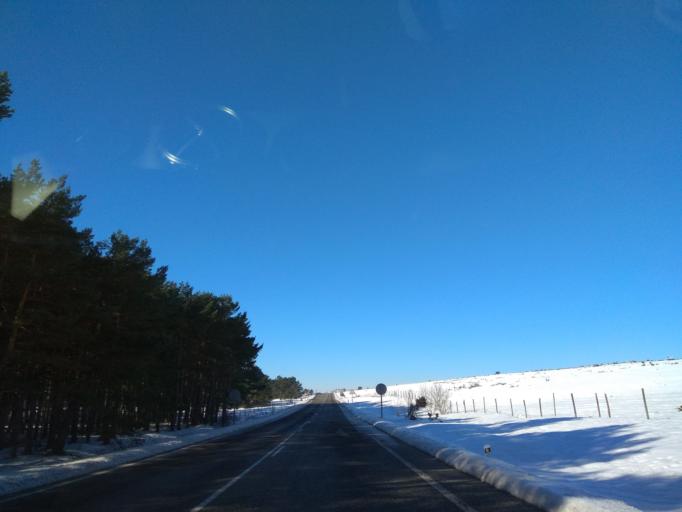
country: ES
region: Castille and Leon
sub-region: Provincia de Burgos
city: Medina de Pomar
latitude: 42.9303
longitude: -3.6514
